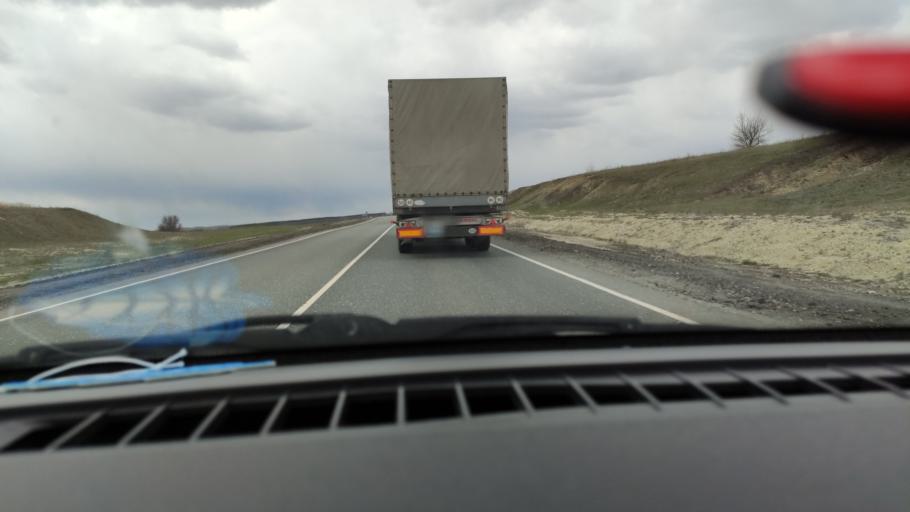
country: RU
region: Saratov
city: Sennoy
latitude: 52.1350
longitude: 46.8697
